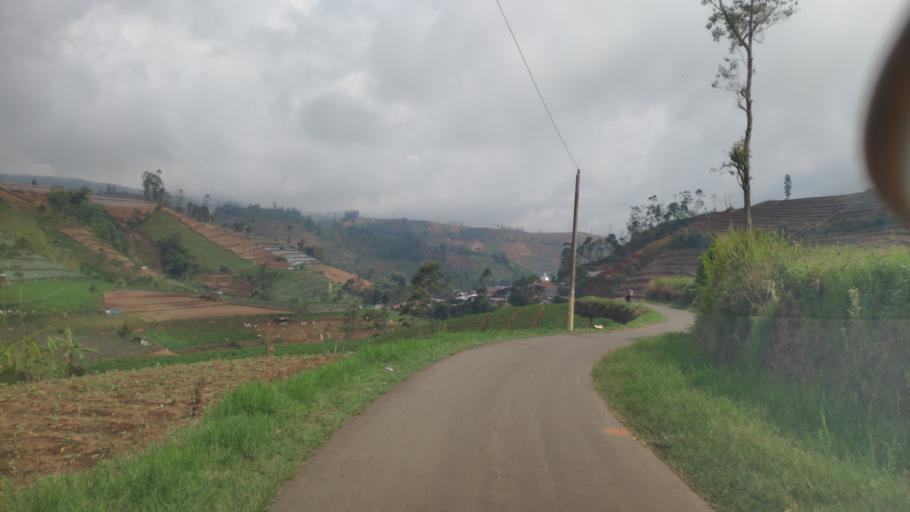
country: ID
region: Central Java
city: Wonosobo
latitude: -7.2282
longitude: 109.8333
